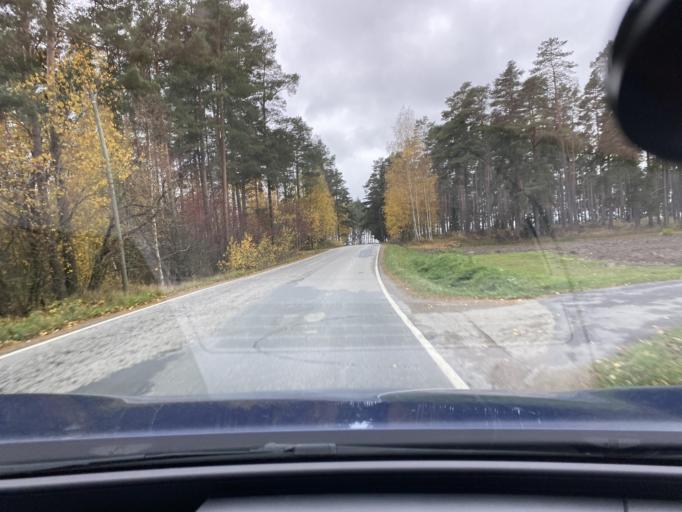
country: FI
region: Varsinais-Suomi
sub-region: Vakka-Suomi
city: Laitila
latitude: 60.9241
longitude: 21.6079
